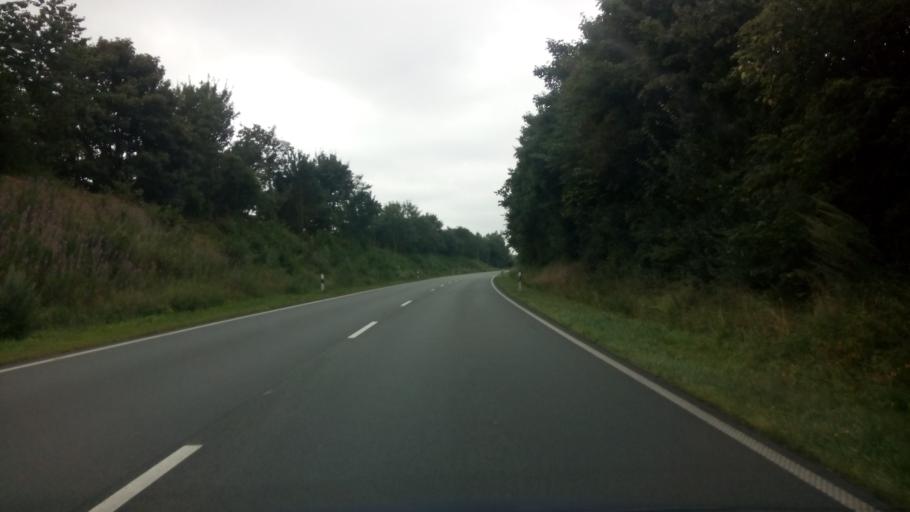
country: DE
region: Lower Saxony
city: Bassum
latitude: 52.8451
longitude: 8.7477
